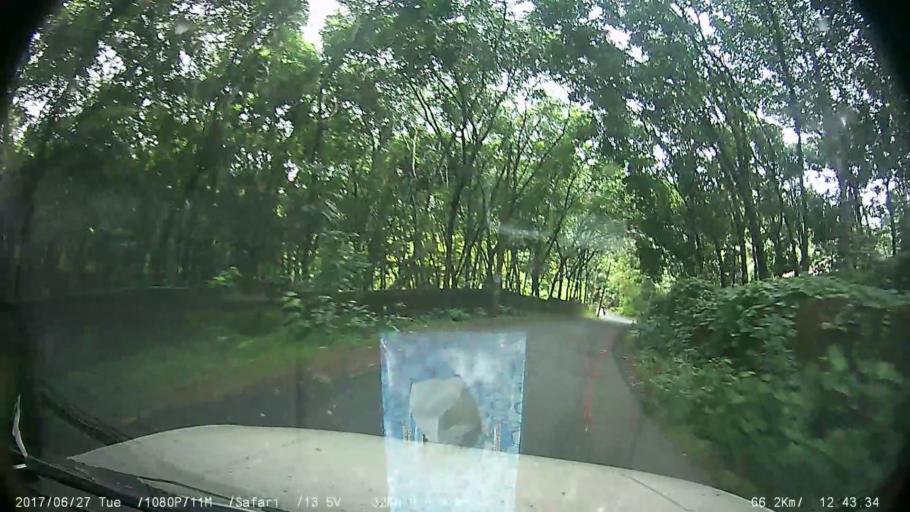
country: IN
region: Kerala
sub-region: Ernakulam
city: Piravam
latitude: 9.7796
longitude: 76.5248
